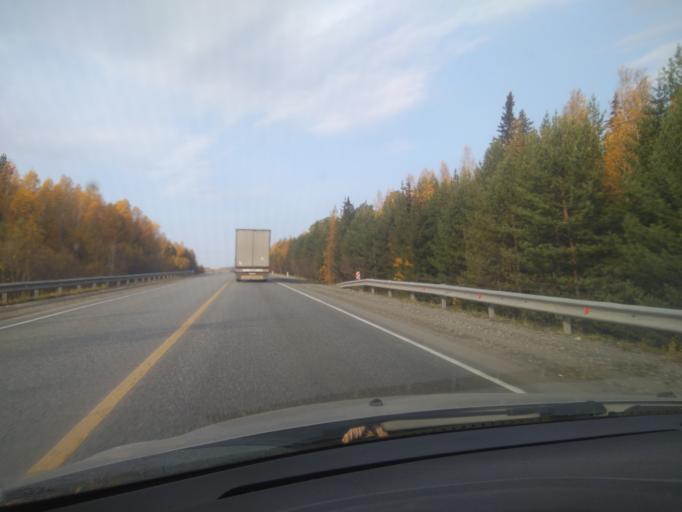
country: RU
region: Sverdlovsk
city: Revda
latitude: 56.8267
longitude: 59.9158
